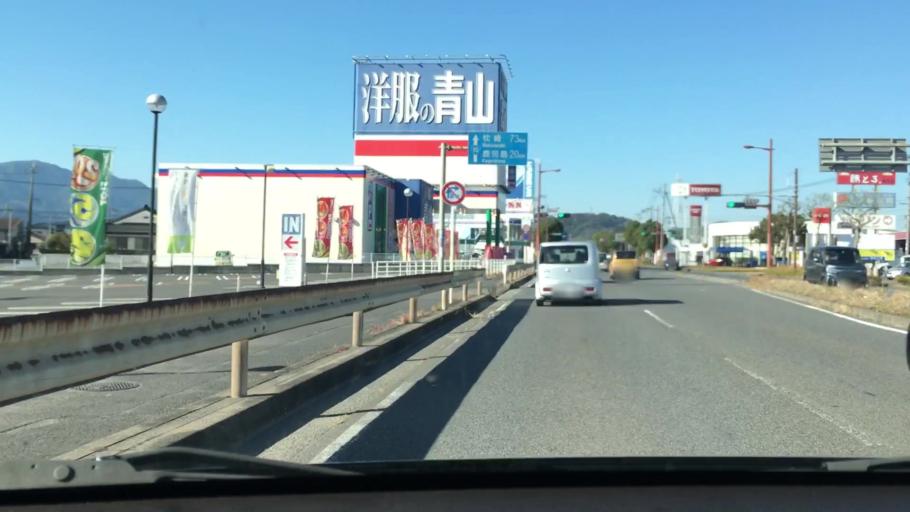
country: JP
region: Kagoshima
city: Kajiki
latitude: 31.7328
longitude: 130.6388
